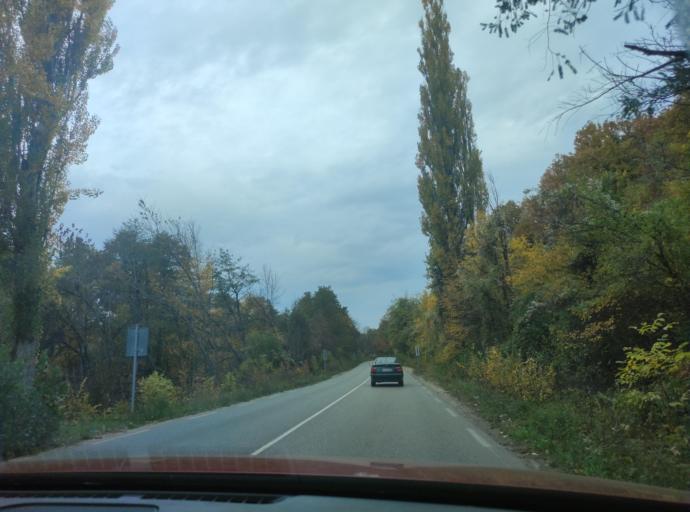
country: BG
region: Montana
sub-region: Obshtina Berkovitsa
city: Berkovitsa
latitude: 43.2652
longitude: 23.1762
